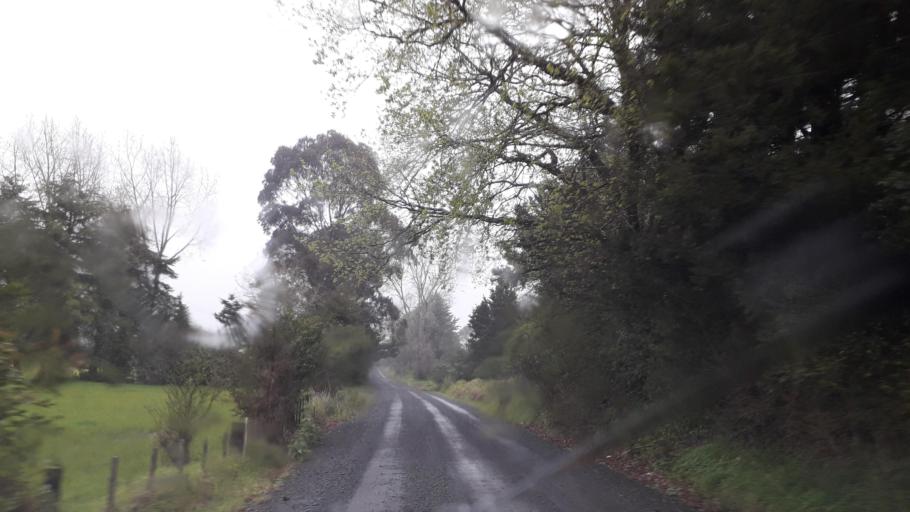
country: NZ
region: Northland
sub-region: Far North District
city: Waimate North
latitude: -35.4910
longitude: 173.7002
